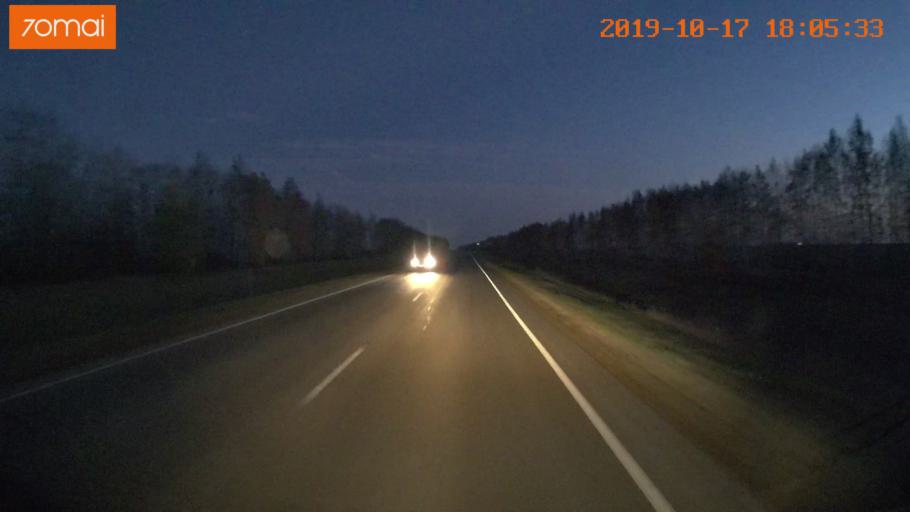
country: RU
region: Tula
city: Kurkino
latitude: 53.4646
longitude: 38.6454
